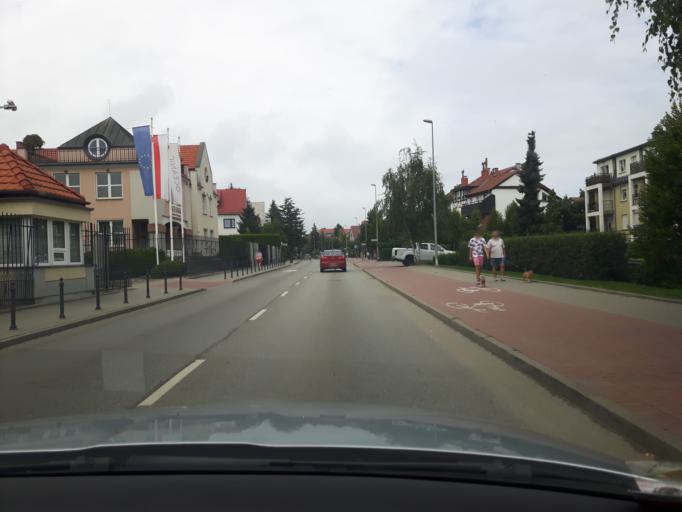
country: PL
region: Pomeranian Voivodeship
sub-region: Sopot
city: Sopot
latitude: 54.4298
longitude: 18.5741
